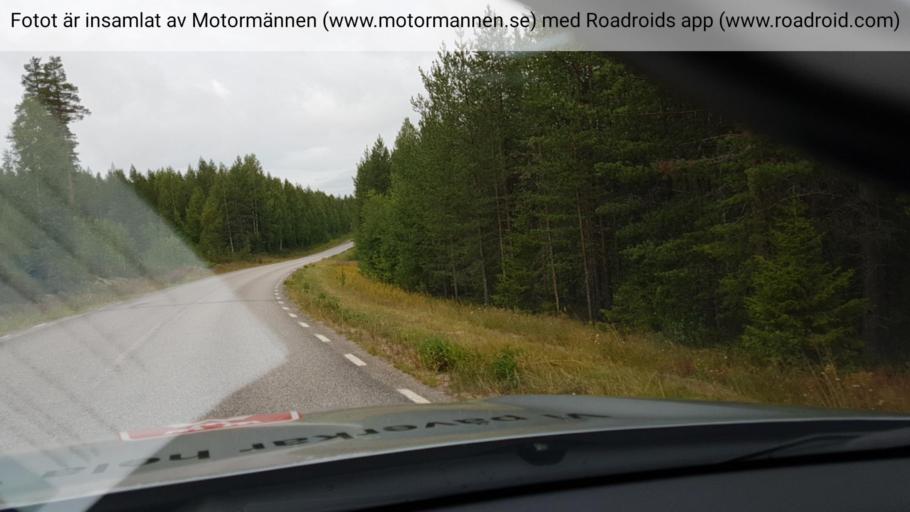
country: SE
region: Norrbotten
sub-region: Bodens Kommun
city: Saevast
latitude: 65.6692
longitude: 21.6922
